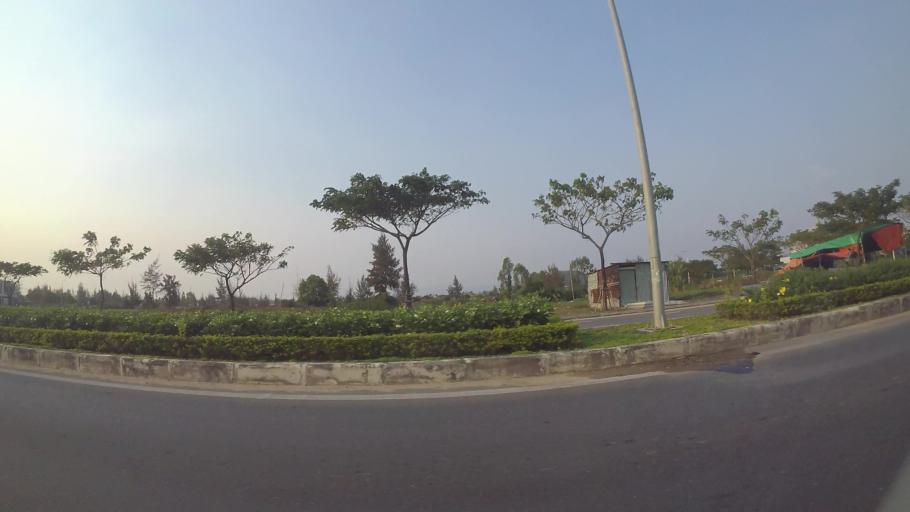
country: VN
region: Da Nang
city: Ngu Hanh Son
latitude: 15.9831
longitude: 108.2517
